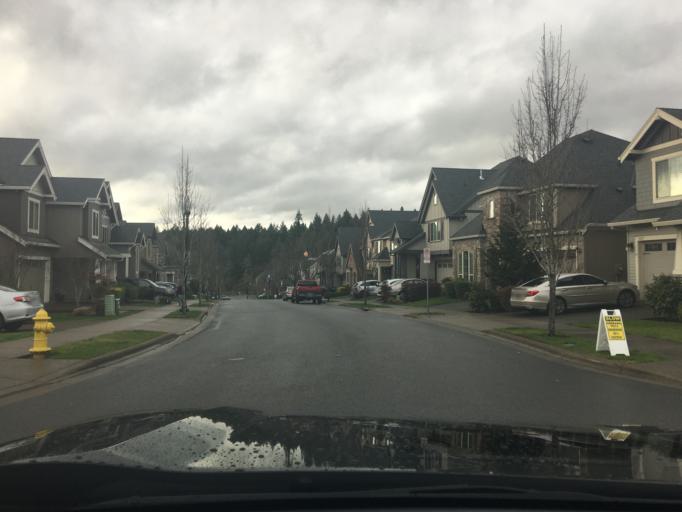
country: US
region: Oregon
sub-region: Washington County
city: Bethany
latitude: 45.5693
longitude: -122.8491
